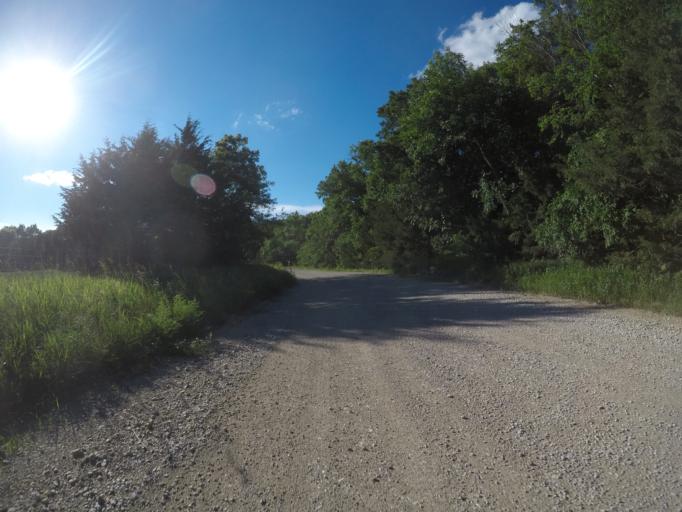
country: US
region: Kansas
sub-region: Riley County
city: Ogden
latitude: 39.2379
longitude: -96.7277
